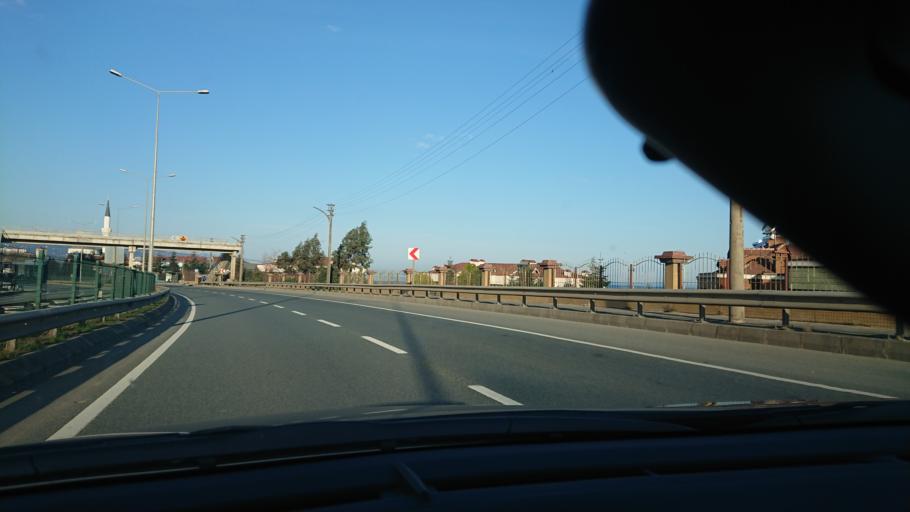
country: TR
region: Trabzon
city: Arsin
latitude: 40.9635
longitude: 39.9928
